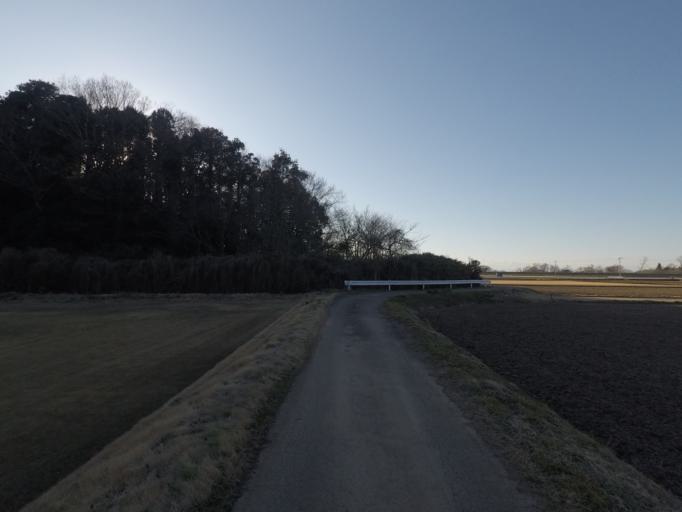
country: JP
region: Ibaraki
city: Ishige
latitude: 36.1351
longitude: 140.0036
